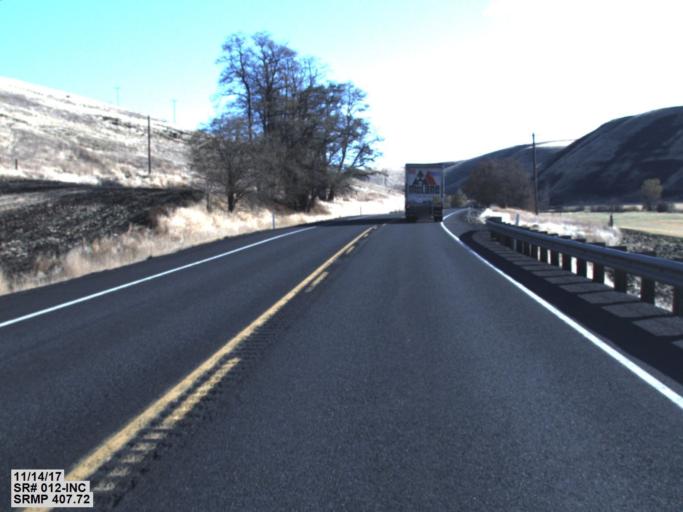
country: US
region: Washington
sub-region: Garfield County
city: Pomeroy
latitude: 46.4689
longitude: -117.5125
